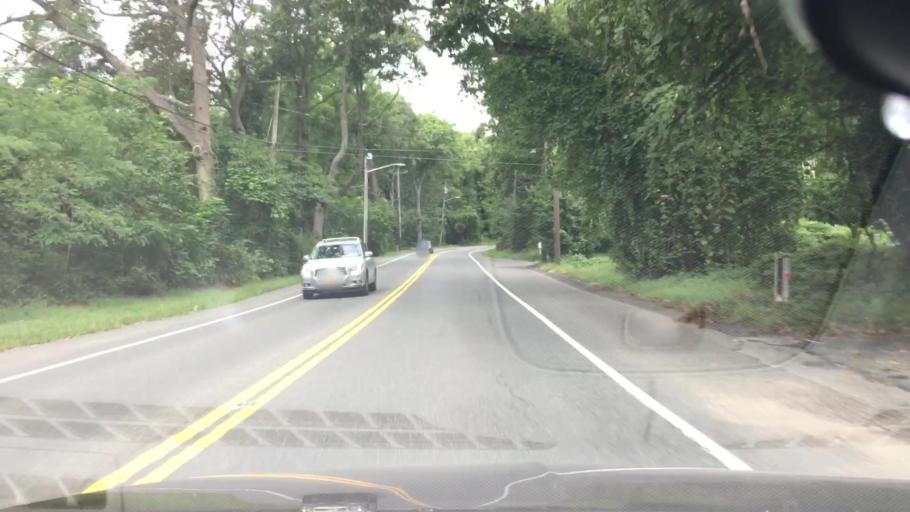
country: US
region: New York
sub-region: Suffolk County
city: Head of the Harbor
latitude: 40.8914
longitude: -73.1542
